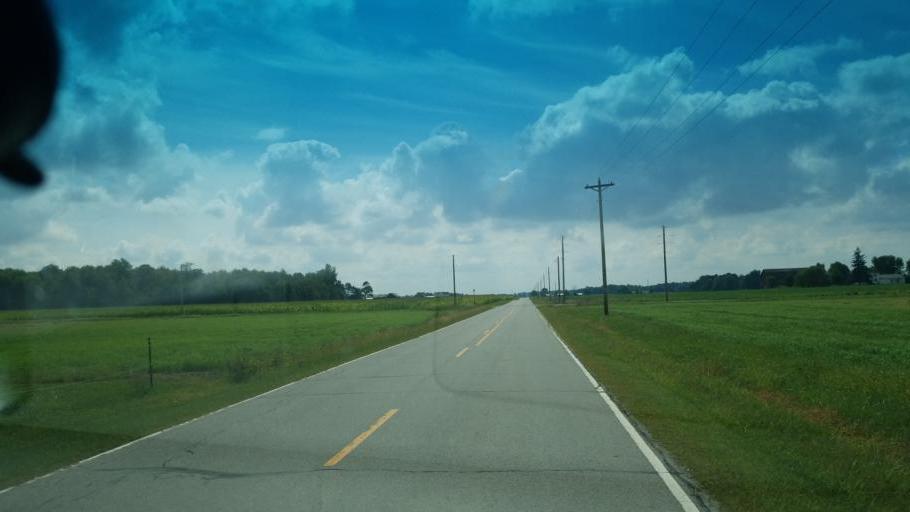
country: US
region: Ohio
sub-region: Crawford County
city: Bucyrus
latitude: 40.9380
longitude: -82.9017
